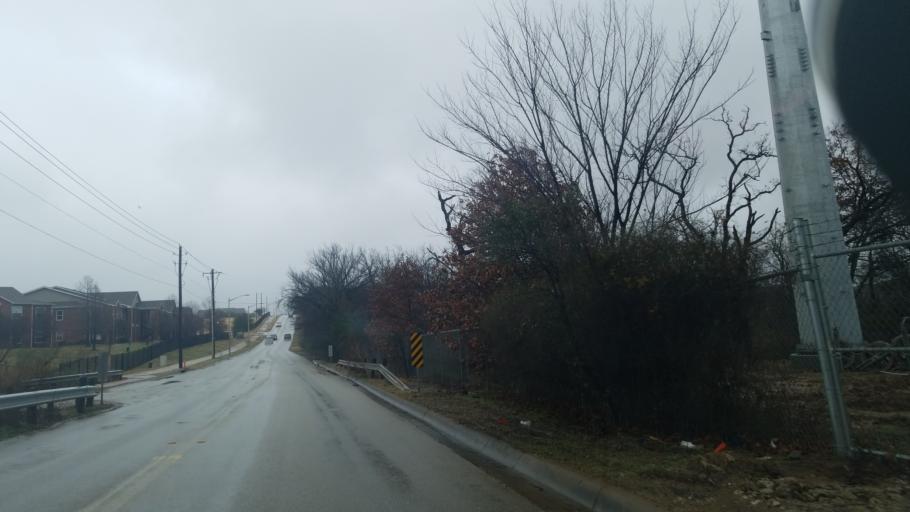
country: US
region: Texas
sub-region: Denton County
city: Corinth
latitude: 33.1785
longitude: -97.0811
